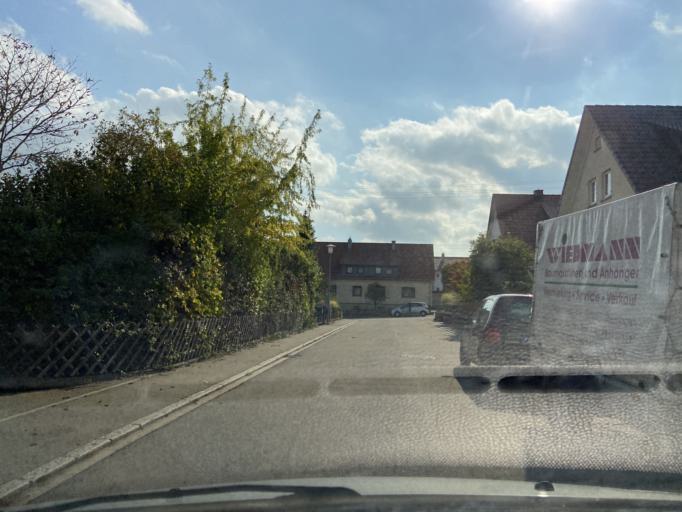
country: DE
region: Baden-Wuerttemberg
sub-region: Tuebingen Region
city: Sigmaringen
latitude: 48.0790
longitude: 9.2191
